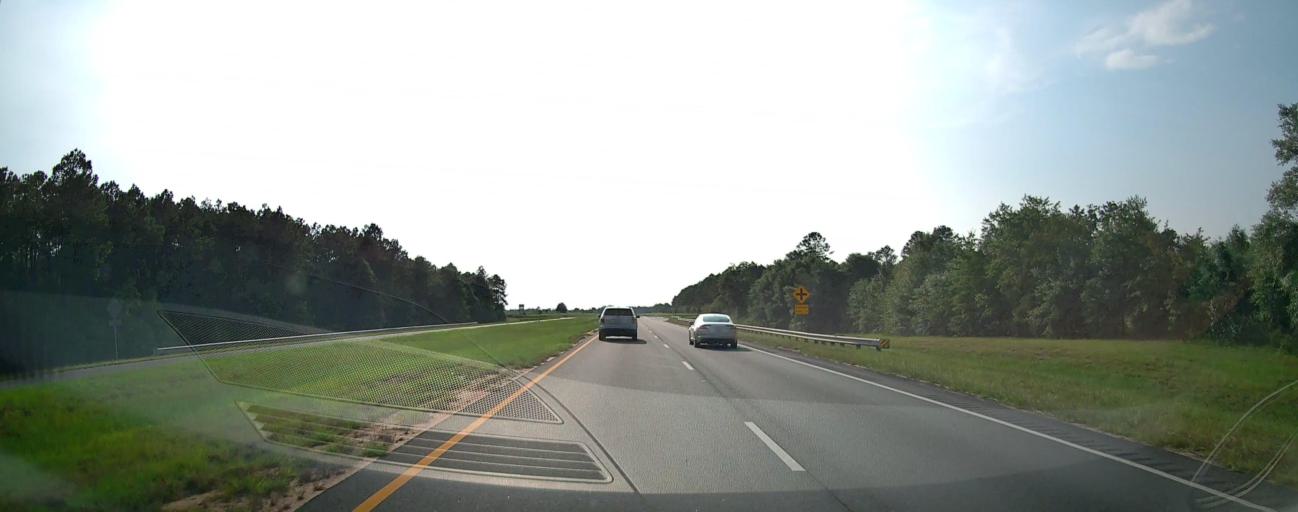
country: US
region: Georgia
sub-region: Taylor County
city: Butler
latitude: 32.5463
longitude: -84.2481
